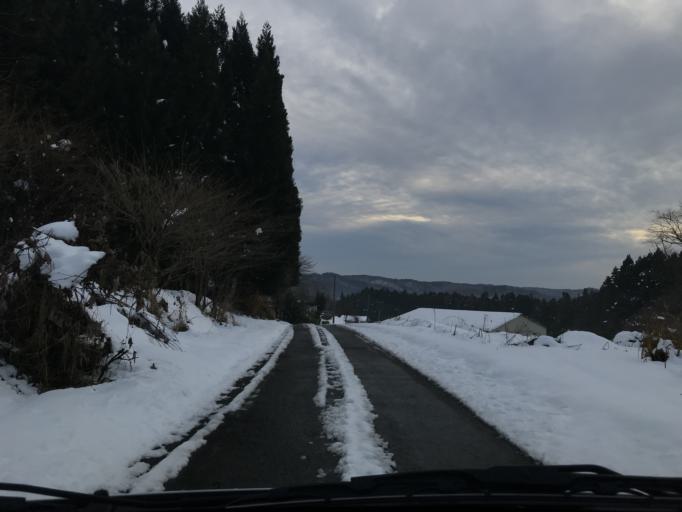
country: JP
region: Iwate
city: Mizusawa
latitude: 39.0502
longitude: 141.0577
